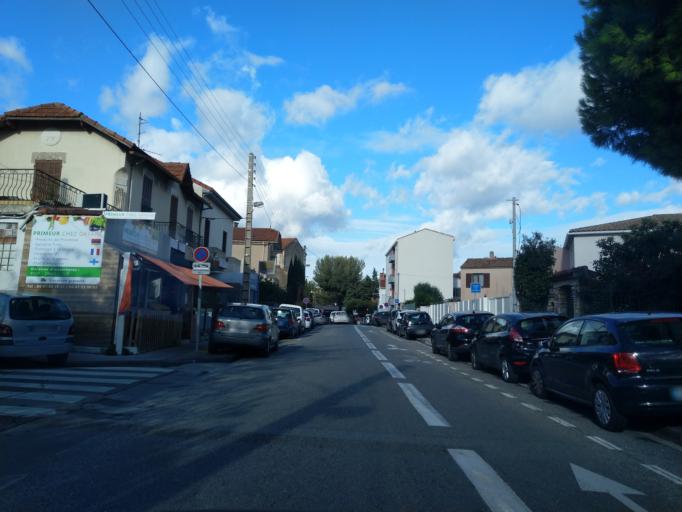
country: FR
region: Provence-Alpes-Cote d'Azur
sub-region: Departement des Bouches-du-Rhone
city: Marseille 12
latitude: 43.3076
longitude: 5.4373
